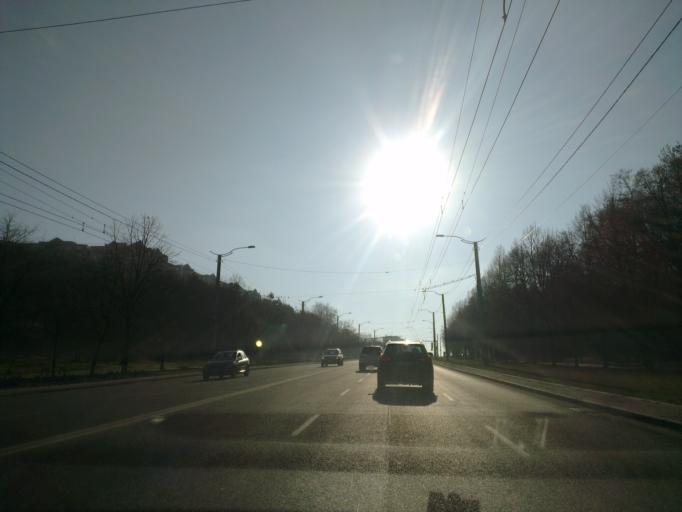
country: MD
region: Chisinau
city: Chisinau
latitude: 47.0411
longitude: 28.8769
